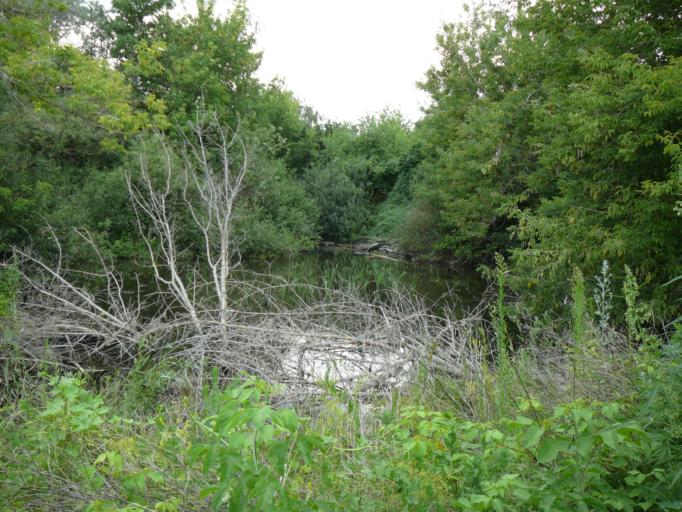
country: RU
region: Saratov
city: Engel's
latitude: 51.4662
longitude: 46.1799
